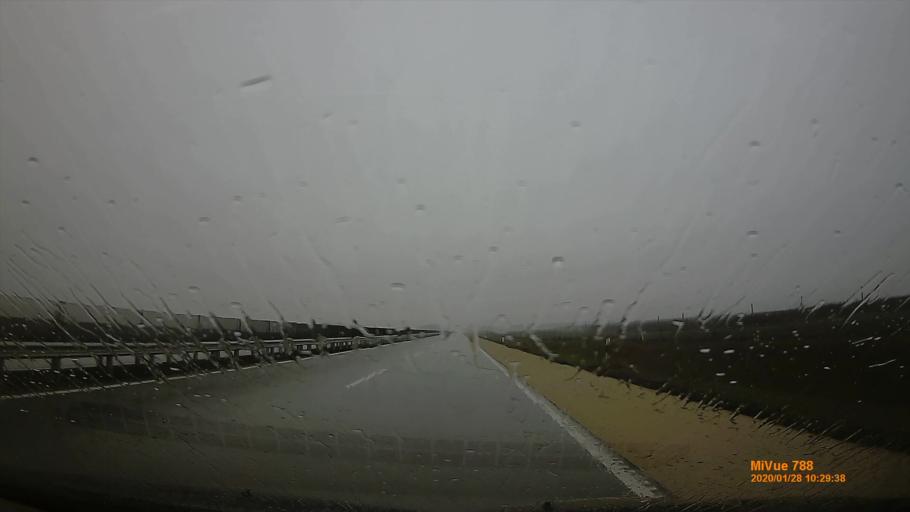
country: HU
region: Pest
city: Pilis
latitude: 47.3259
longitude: 19.5305
